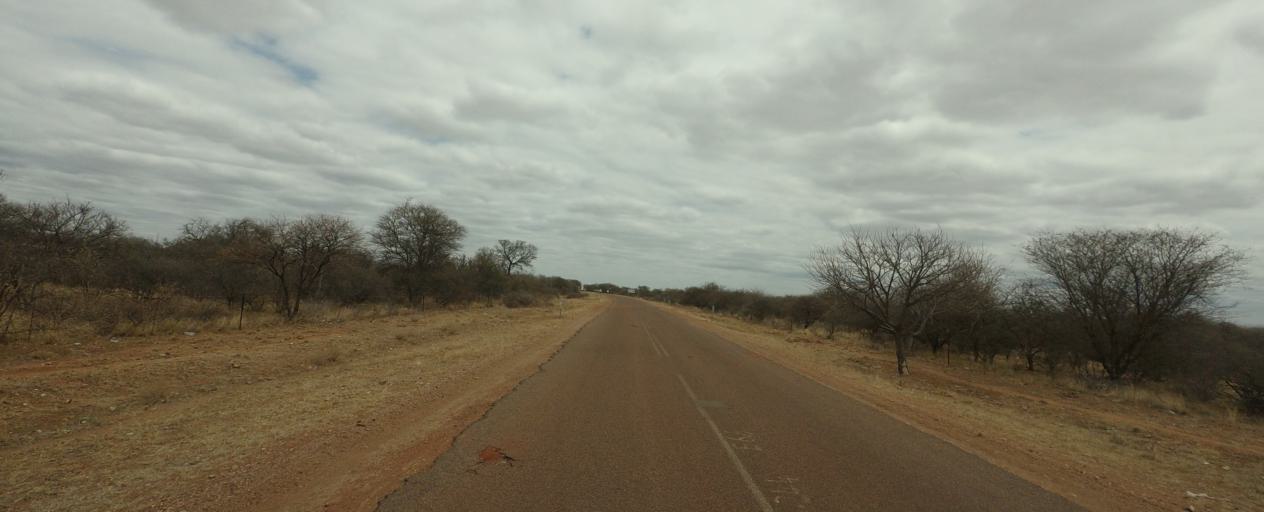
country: BW
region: Central
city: Makobeng
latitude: -22.8447
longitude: 28.2061
